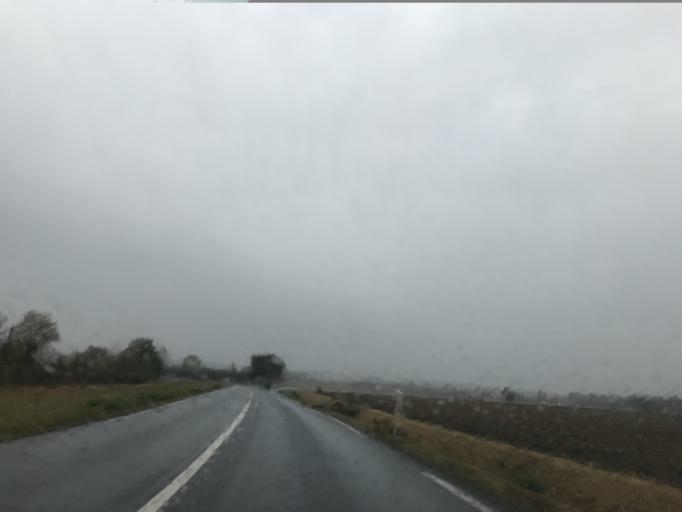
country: FR
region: Auvergne
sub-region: Departement du Puy-de-Dome
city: Dallet
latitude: 45.7800
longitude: 3.2488
